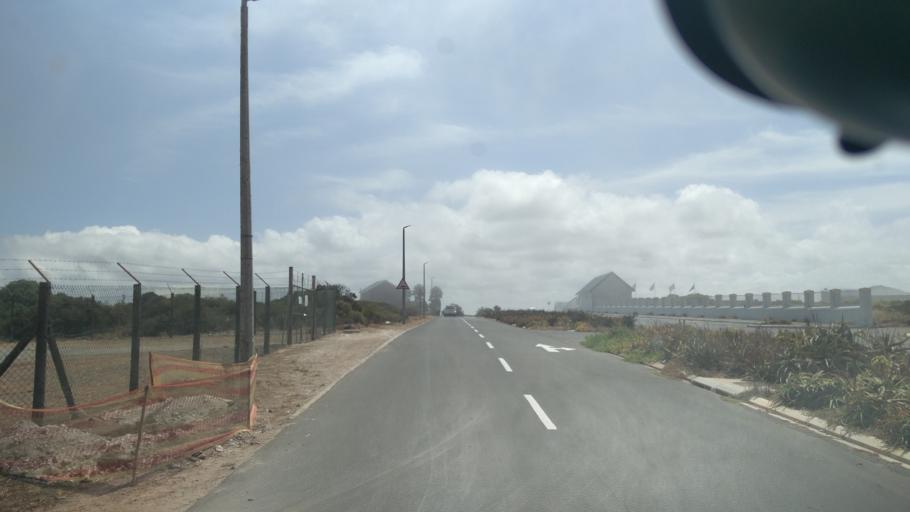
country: ZA
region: Western Cape
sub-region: City of Cape Town
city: Atlantis
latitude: -33.3485
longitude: 18.1559
